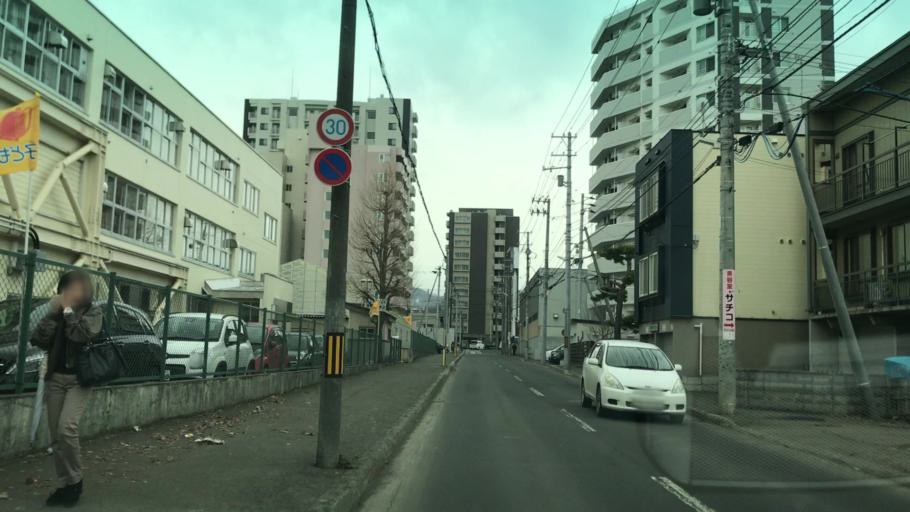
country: JP
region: Hokkaido
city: Sapporo
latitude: 43.0753
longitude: 141.2991
